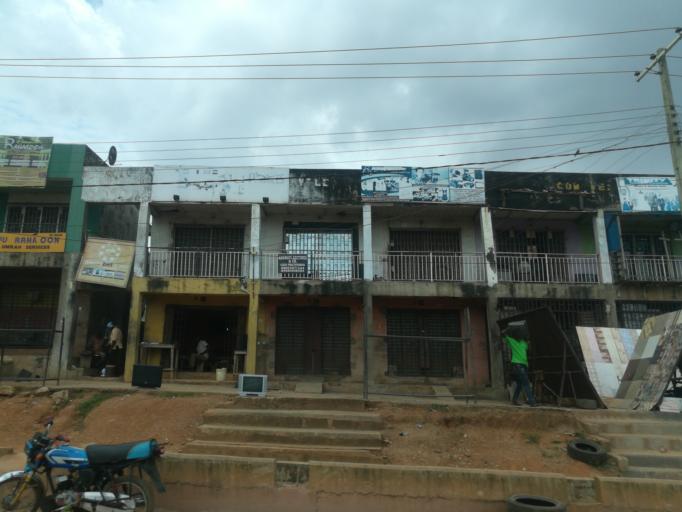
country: NG
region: Oyo
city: Ibadan
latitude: 7.4037
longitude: 3.9342
